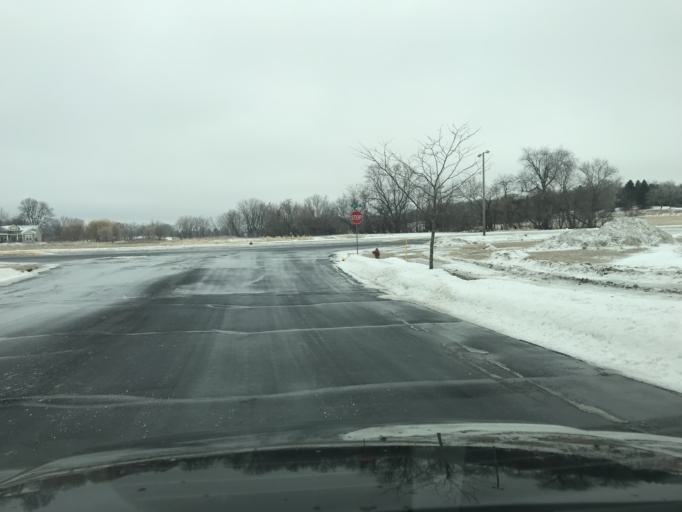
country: US
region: Wisconsin
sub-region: Dane County
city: Cottage Grove
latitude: 43.0887
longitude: -89.2157
